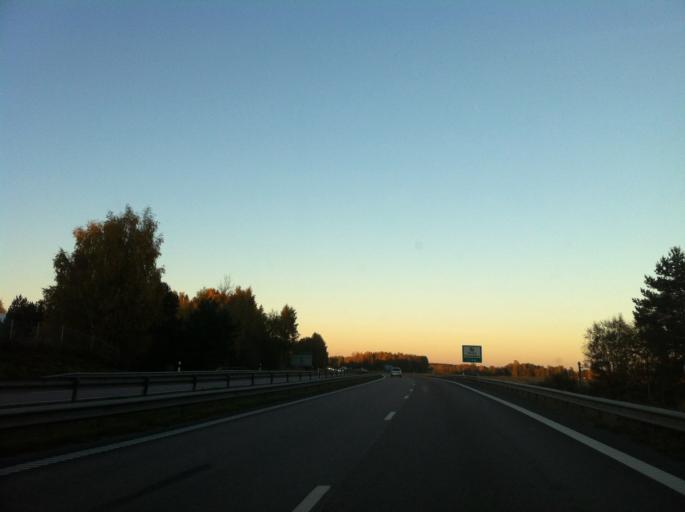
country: SE
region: Gaevleborg
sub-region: Gavle Kommun
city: Valbo
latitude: 60.6357
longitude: 17.0075
